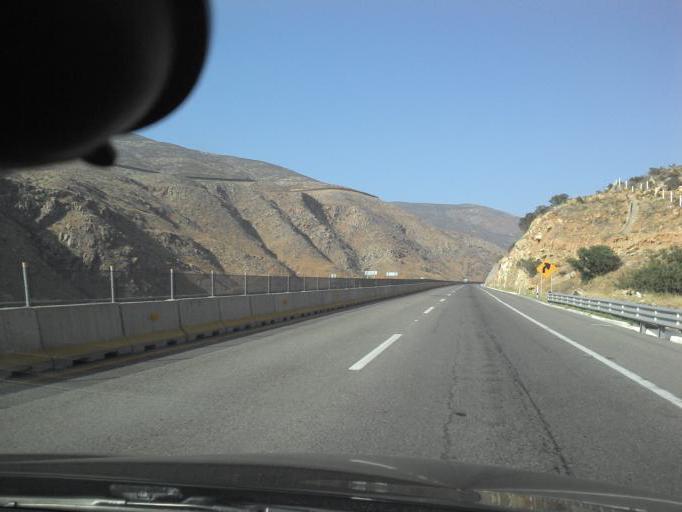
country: MX
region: Baja California
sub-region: Tijuana
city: Ejido Javier Rojo Gomez
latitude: 32.5482
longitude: -116.8491
